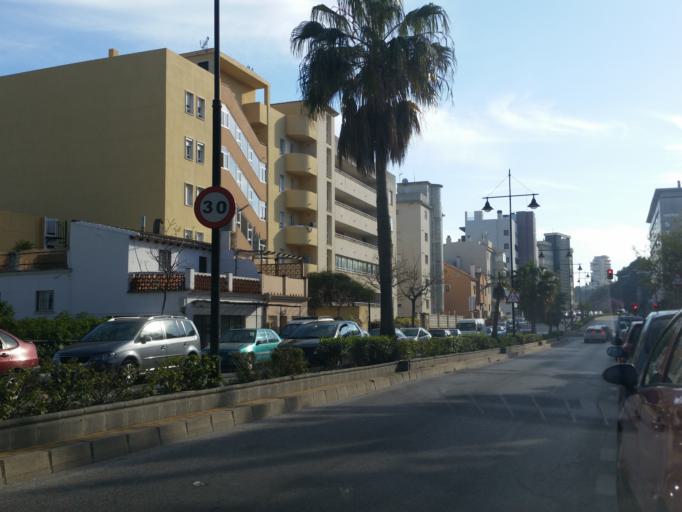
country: ES
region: Andalusia
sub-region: Provincia de Malaga
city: Benalmadena
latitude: 36.5709
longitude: -4.5921
